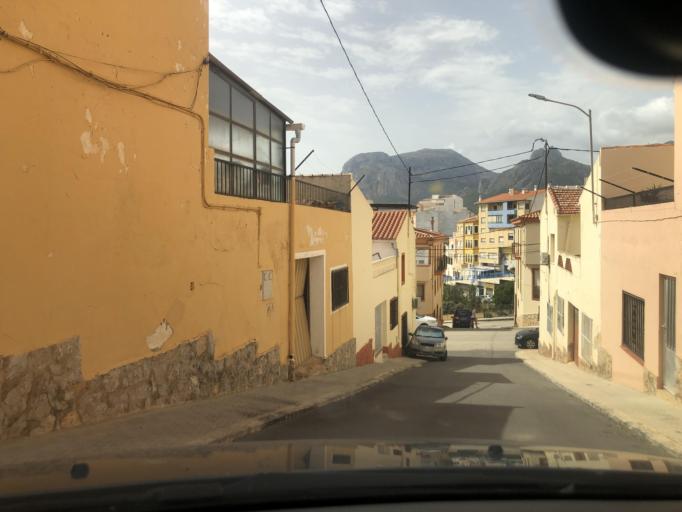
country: ES
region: Valencia
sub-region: Provincia de Alicante
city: Callosa d'En Sarria
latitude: 38.6523
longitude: -0.1195
